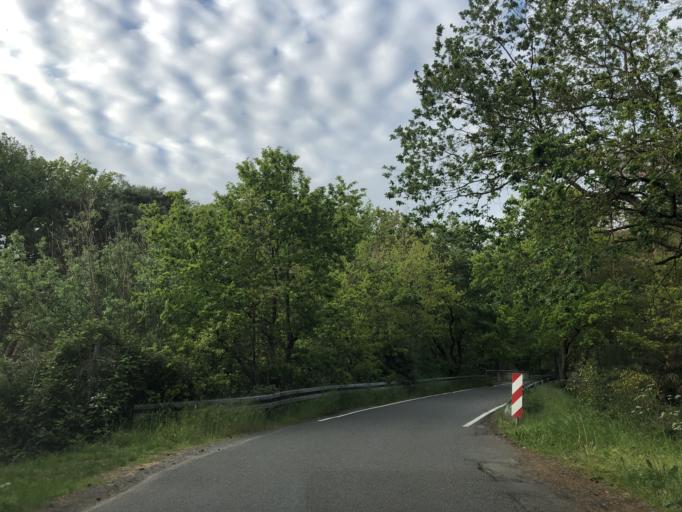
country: DE
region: Hesse
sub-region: Regierungsbezirk Darmstadt
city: Erzhausen
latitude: 49.9460
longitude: 8.6039
